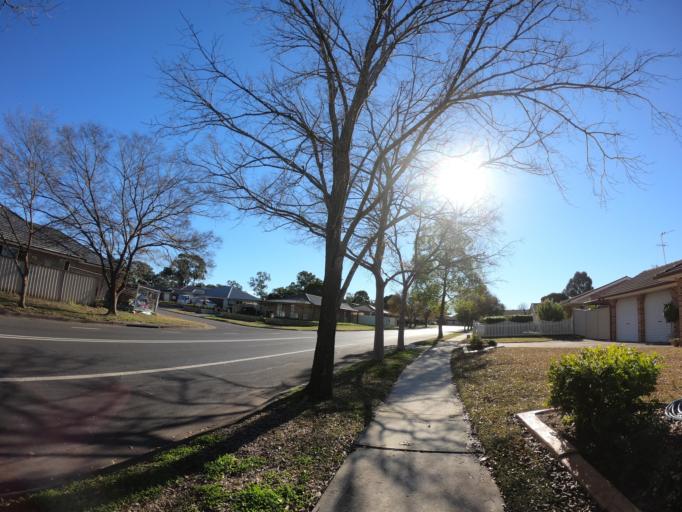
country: AU
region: New South Wales
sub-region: Hawkesbury
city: South Windsor
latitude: -33.6366
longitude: 150.7898
